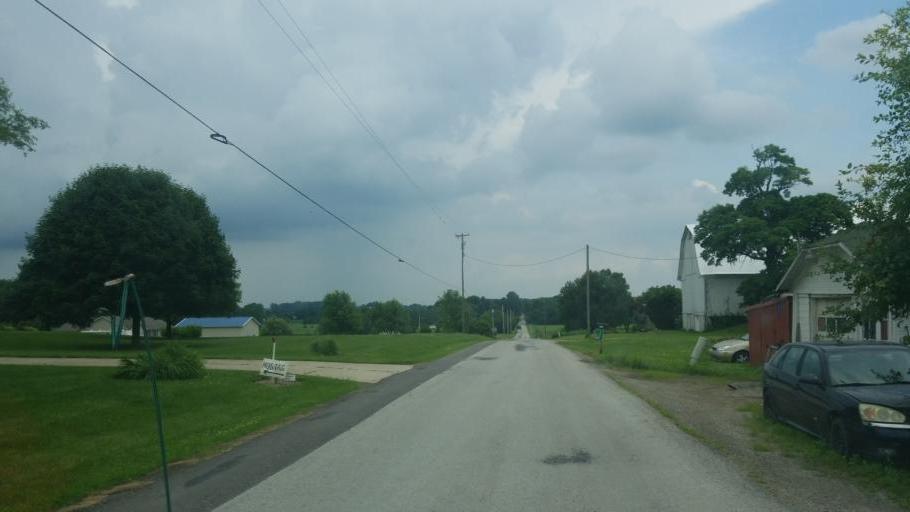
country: US
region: Ohio
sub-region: Wayne County
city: Smithville
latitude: 40.8942
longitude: -81.9159
